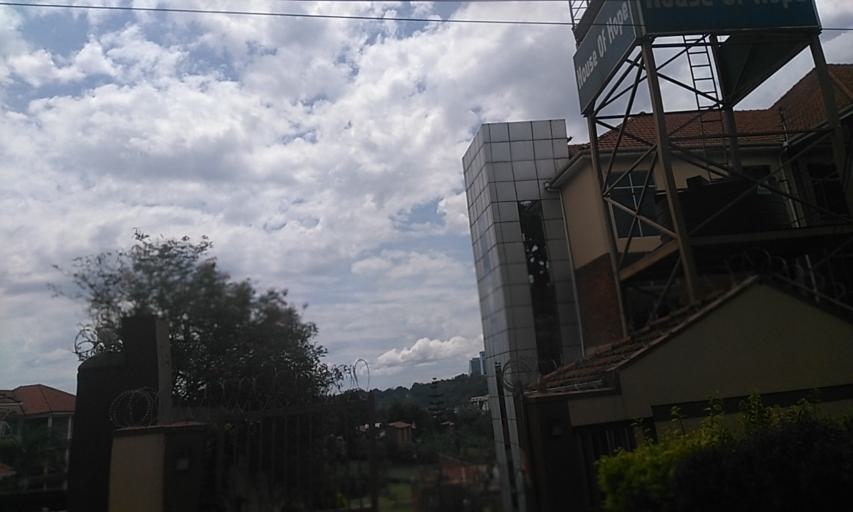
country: UG
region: Central Region
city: Kampala Central Division
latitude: 0.3373
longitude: 32.5863
